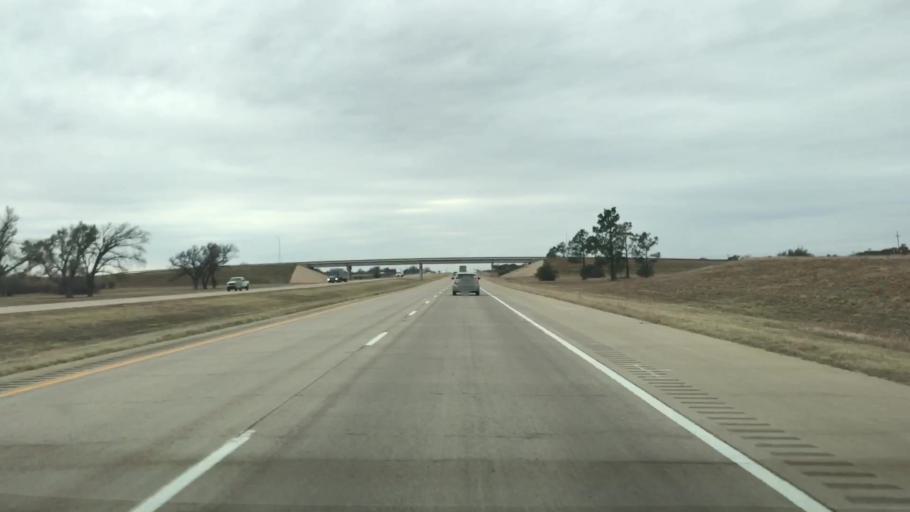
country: US
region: Texas
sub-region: Wheeler County
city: Shamrock
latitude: 35.2270
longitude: -100.1622
